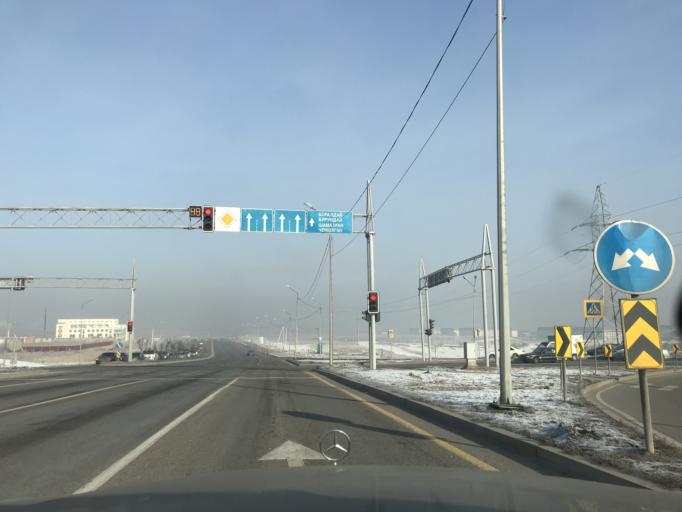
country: KZ
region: Almaty Oblysy
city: Burunday
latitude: 43.3130
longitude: 76.8342
